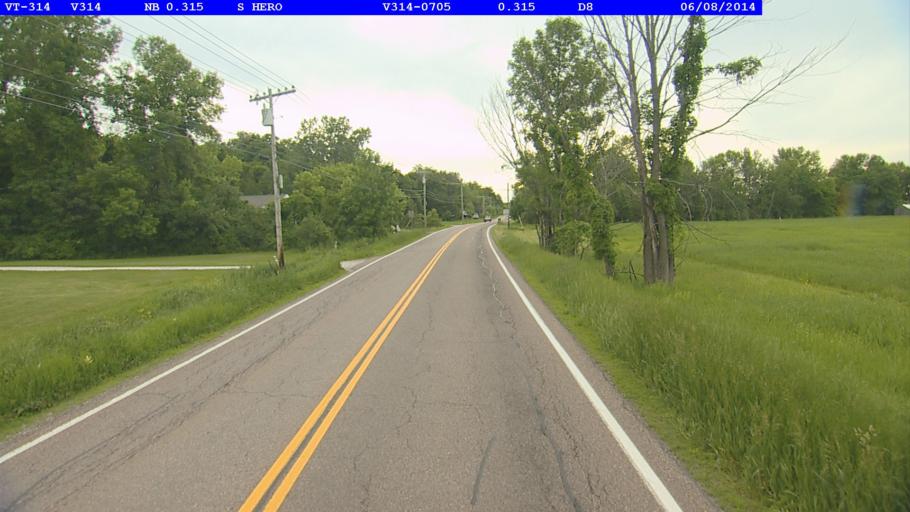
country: US
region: New York
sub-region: Clinton County
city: Cumberland Head
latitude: 44.6660
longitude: -73.3287
